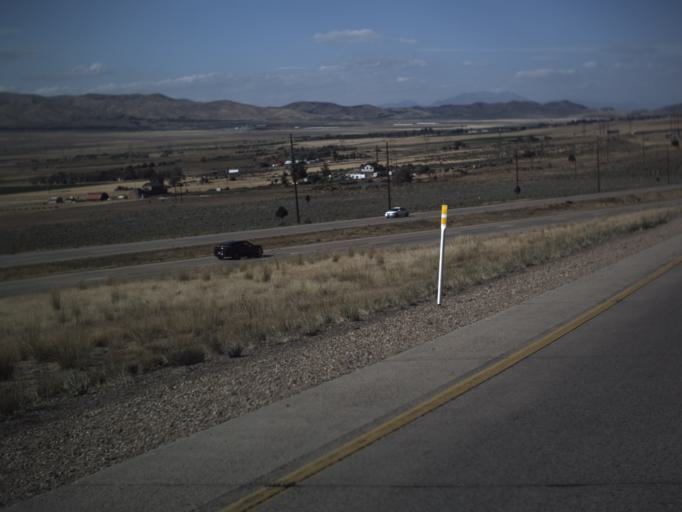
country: US
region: Utah
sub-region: Juab County
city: Nephi
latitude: 39.7521
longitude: -111.8341
